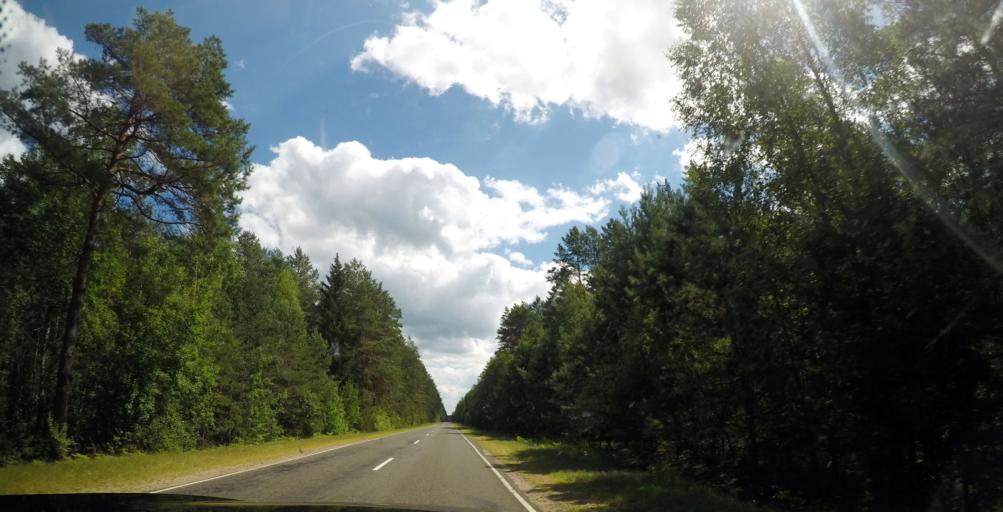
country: LT
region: Alytaus apskritis
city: Druskininkai
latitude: 53.8590
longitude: 24.1812
